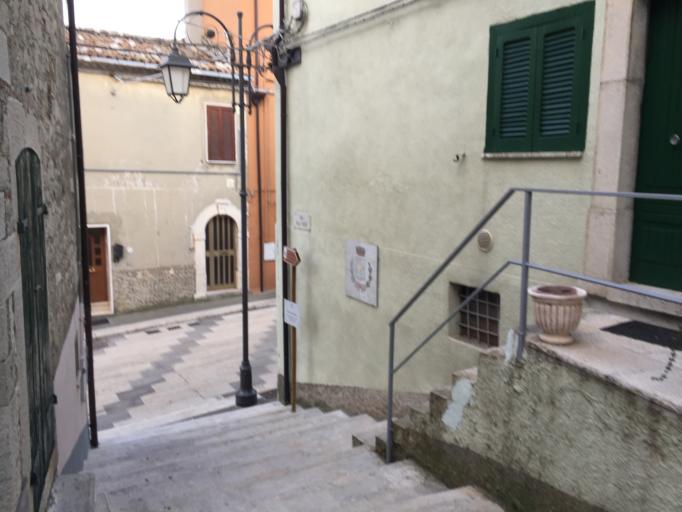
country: IT
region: Molise
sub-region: Provincia di Campobasso
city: Guardiaregia
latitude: 41.4348
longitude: 14.5415
